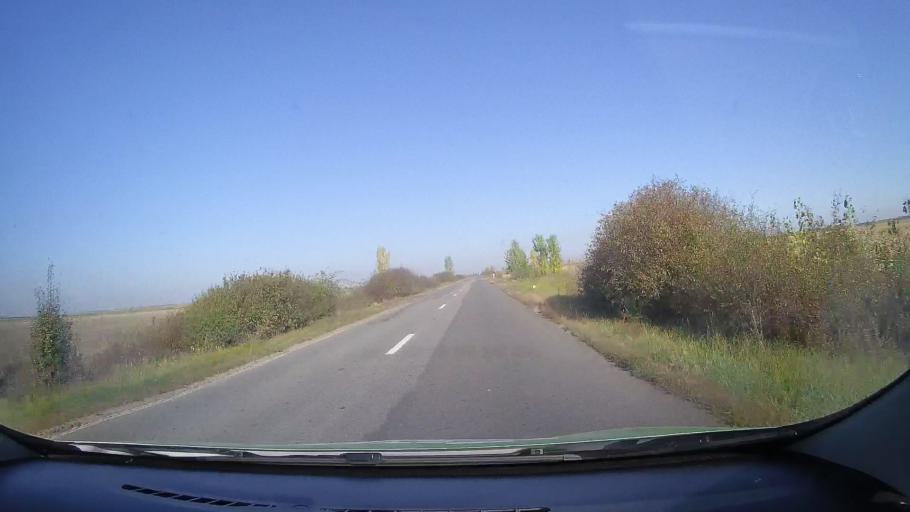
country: RO
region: Satu Mare
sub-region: Comuna Cauas
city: Cauas
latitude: 47.5263
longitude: 22.5683
